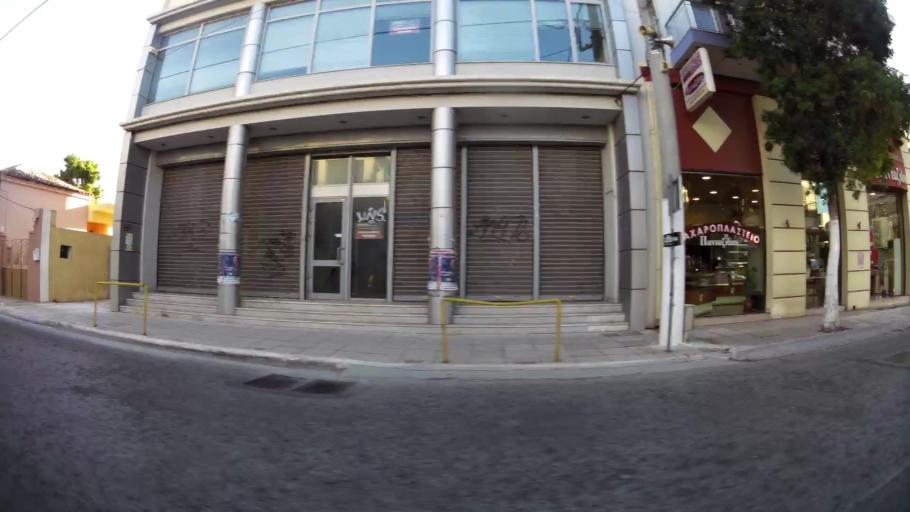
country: GR
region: Attica
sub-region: Nomarchia Anatolikis Attikis
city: Koropi
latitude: 37.9050
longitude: 23.8728
